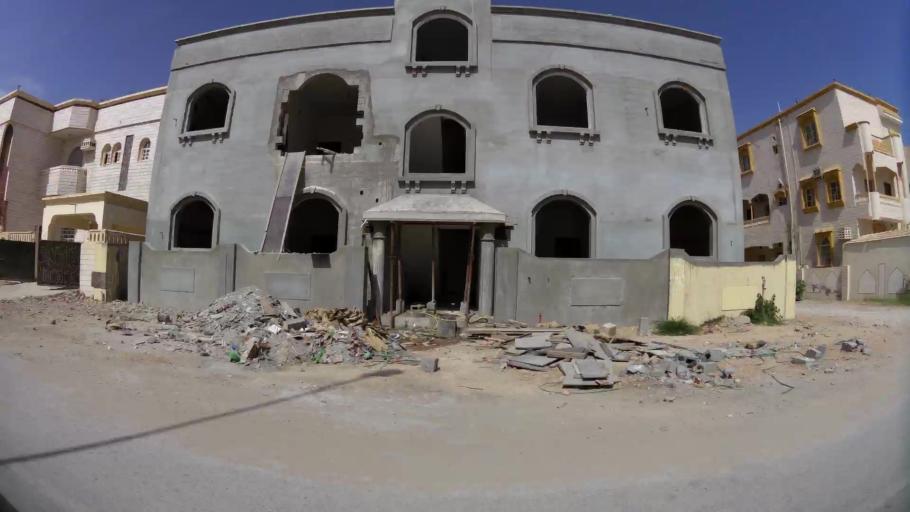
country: OM
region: Zufar
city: Salalah
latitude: 17.0463
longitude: 54.1540
